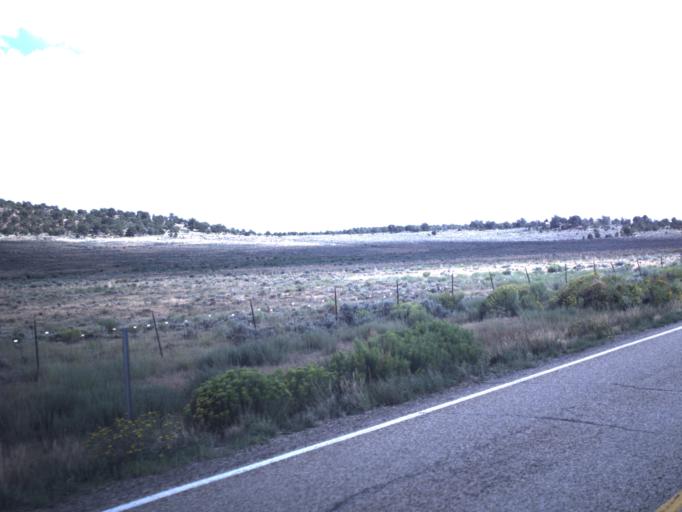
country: US
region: Utah
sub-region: Duchesne County
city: Duchesne
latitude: 40.2524
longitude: -110.7106
